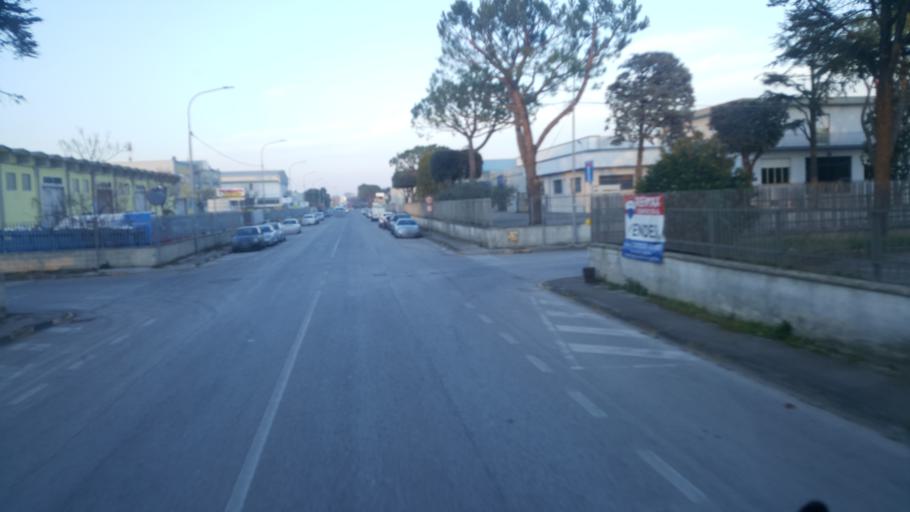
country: IT
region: The Marches
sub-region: Provincia di Ancona
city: Falconara Marittima
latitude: 43.6173
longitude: 13.3727
